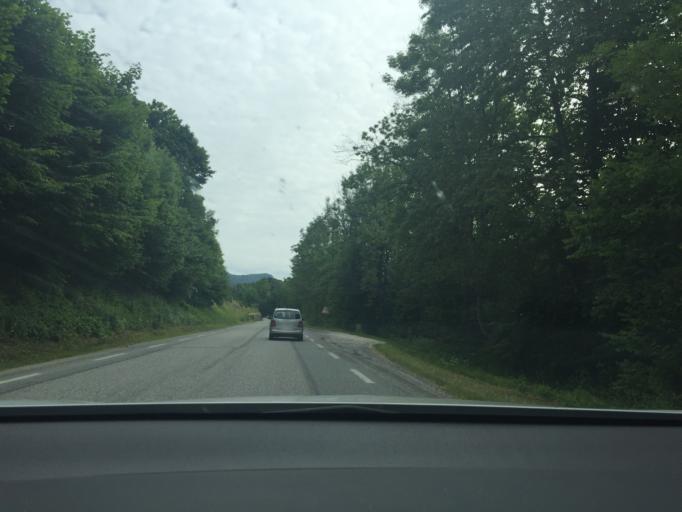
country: FR
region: Rhone-Alpes
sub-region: Departement de la Savoie
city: Vimines
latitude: 45.4938
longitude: 5.8365
